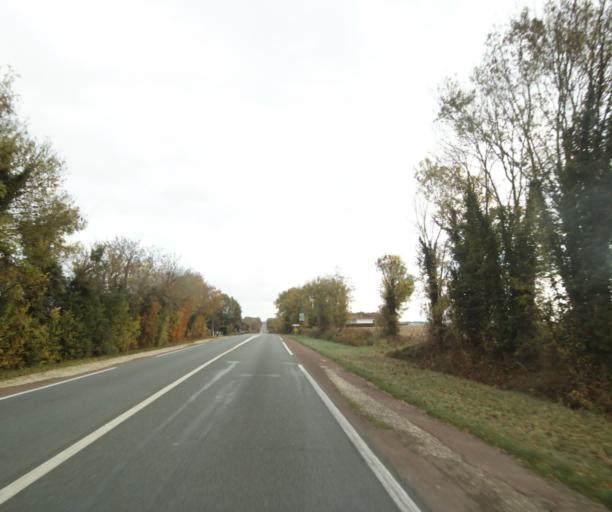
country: FR
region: Poitou-Charentes
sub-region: Departement de la Charente-Maritime
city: Saint-Georges-des-Coteaux
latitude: 45.7662
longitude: -0.6783
